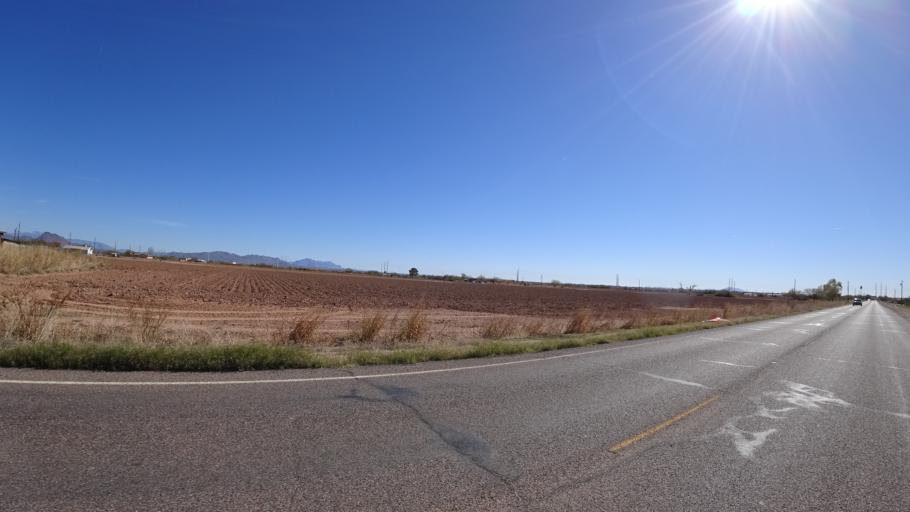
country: US
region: Arizona
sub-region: Maricopa County
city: Mesa
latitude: 33.4938
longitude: -111.8222
